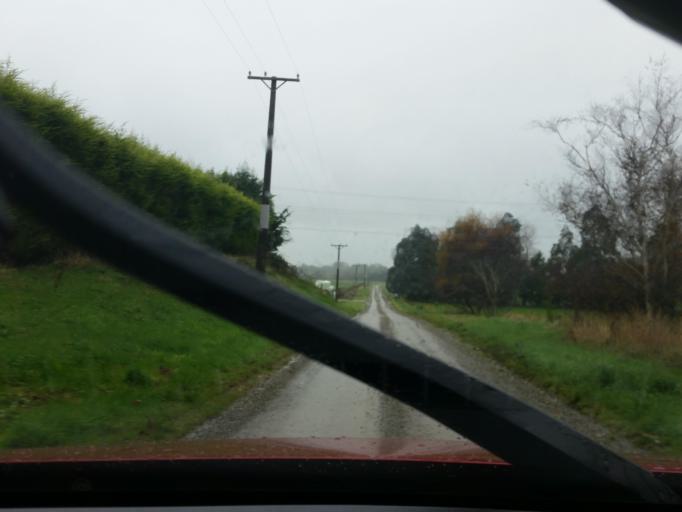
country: NZ
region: Southland
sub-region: Invercargill City
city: Invercargill
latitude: -46.3399
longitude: 168.3952
